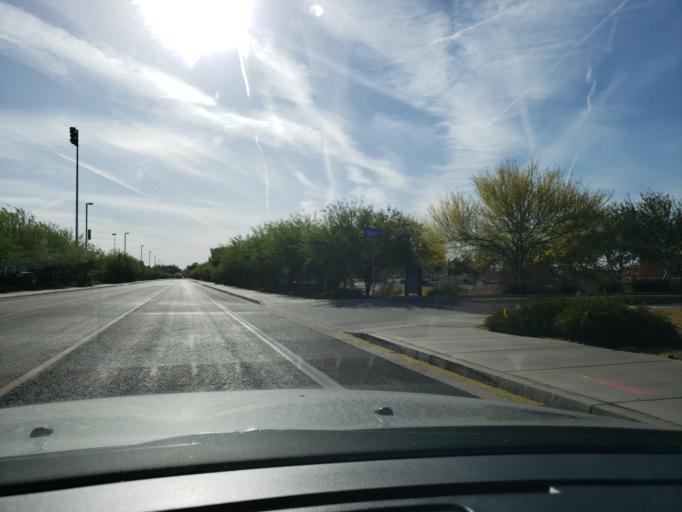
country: US
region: Arizona
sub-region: Maricopa County
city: Queen Creek
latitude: 33.3096
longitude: -111.6734
